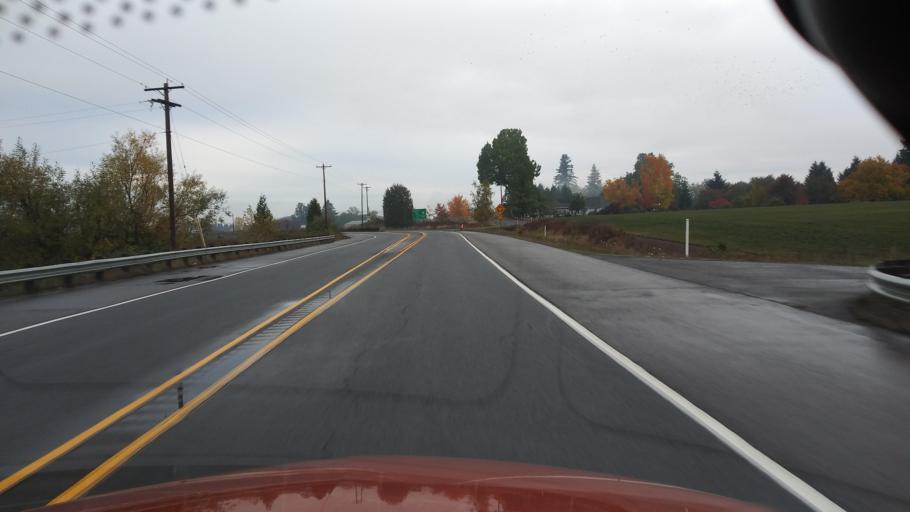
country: US
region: Oregon
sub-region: Washington County
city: Cornelius
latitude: 45.5494
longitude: -123.0616
